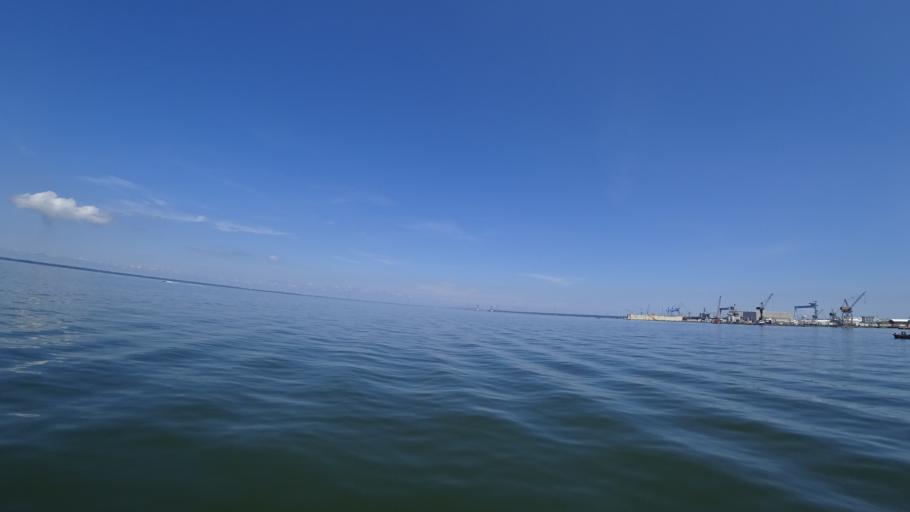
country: US
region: Virginia
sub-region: City of Newport News
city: Newport News
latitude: 36.9768
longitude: -76.4436
